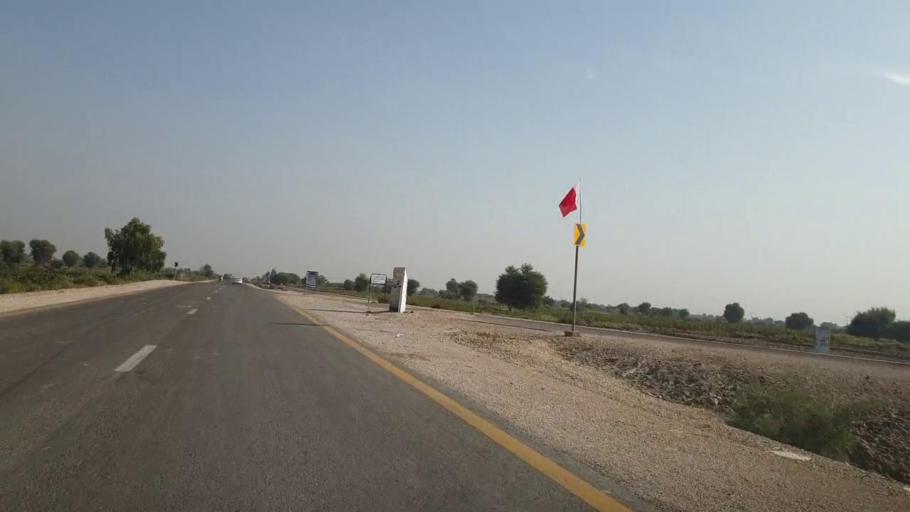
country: PK
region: Sindh
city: Sehwan
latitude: 26.4548
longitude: 67.8086
